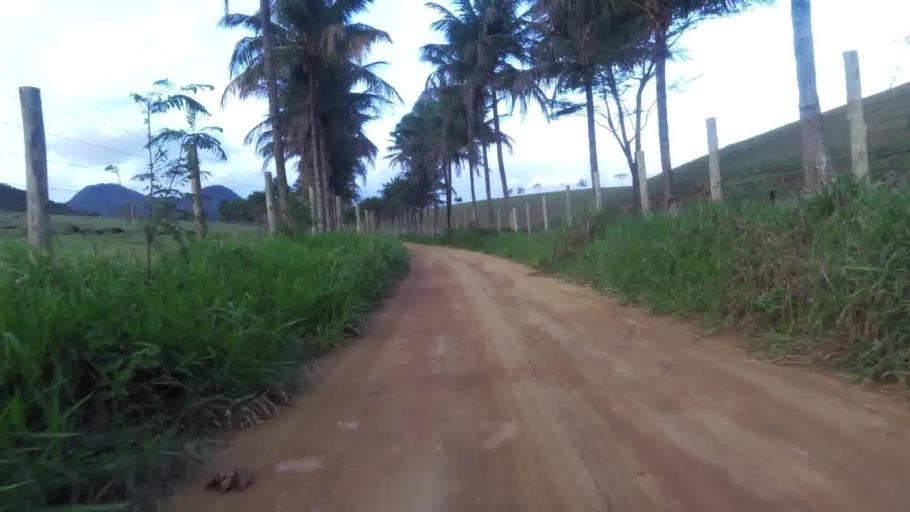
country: BR
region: Espirito Santo
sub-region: Guarapari
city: Guarapari
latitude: -20.6776
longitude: -40.6193
